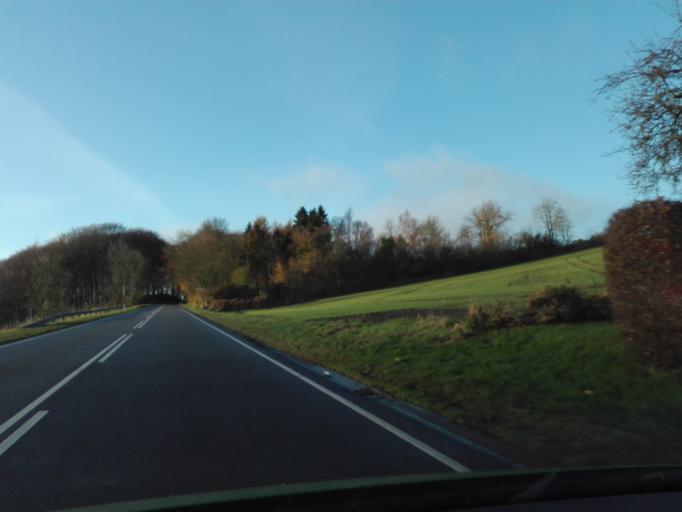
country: DK
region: Central Jutland
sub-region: Skanderborg Kommune
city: Skanderborg
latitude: 56.0592
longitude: 9.9070
